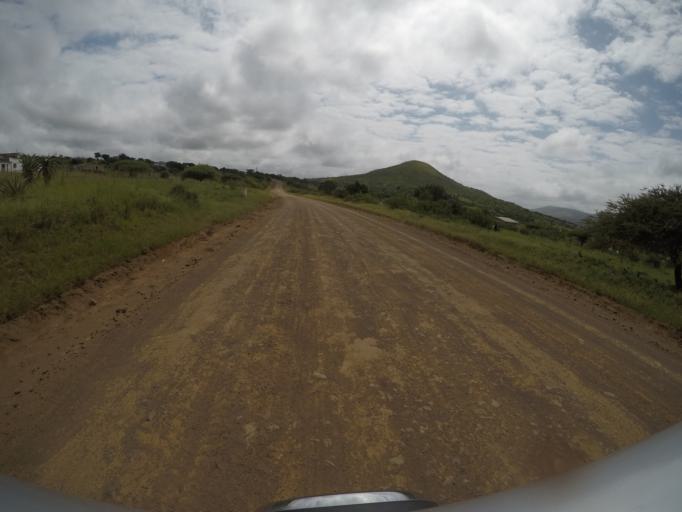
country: ZA
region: KwaZulu-Natal
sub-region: uThungulu District Municipality
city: Empangeni
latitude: -28.6074
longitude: 31.8478
